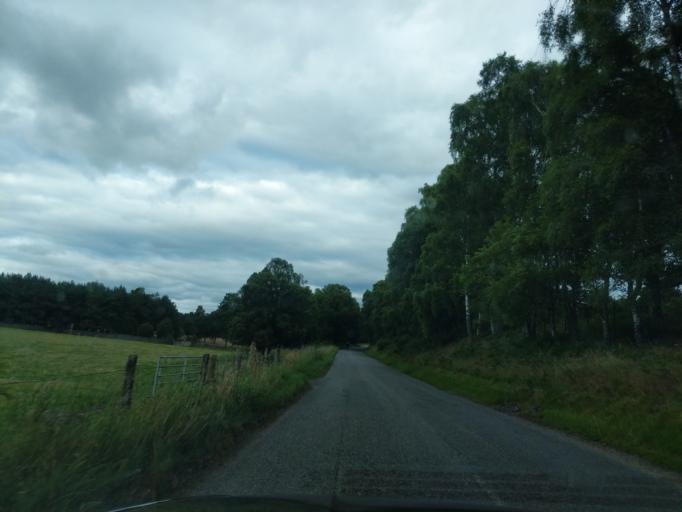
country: GB
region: Scotland
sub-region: Aberdeenshire
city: Aboyne
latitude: 57.0698
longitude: -2.8271
